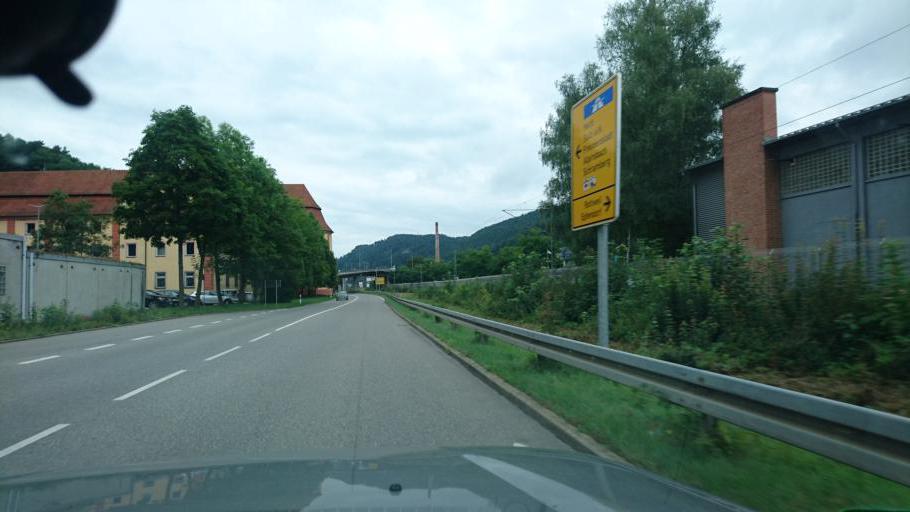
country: DE
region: Baden-Wuerttemberg
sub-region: Freiburg Region
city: Oberndorf
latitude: 48.2911
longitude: 8.5757
